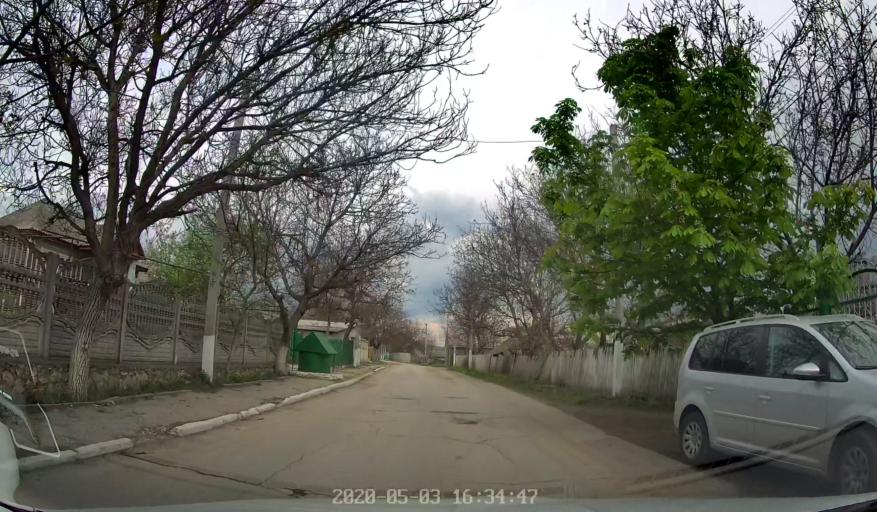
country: MD
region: Calarasi
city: Calarasi
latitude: 47.1908
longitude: 28.3500
